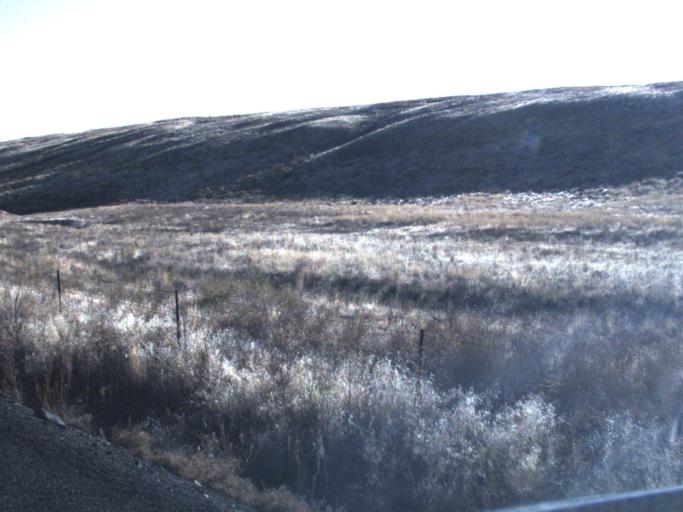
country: US
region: Washington
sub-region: Adams County
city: Ritzville
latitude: 46.7857
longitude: -118.2879
